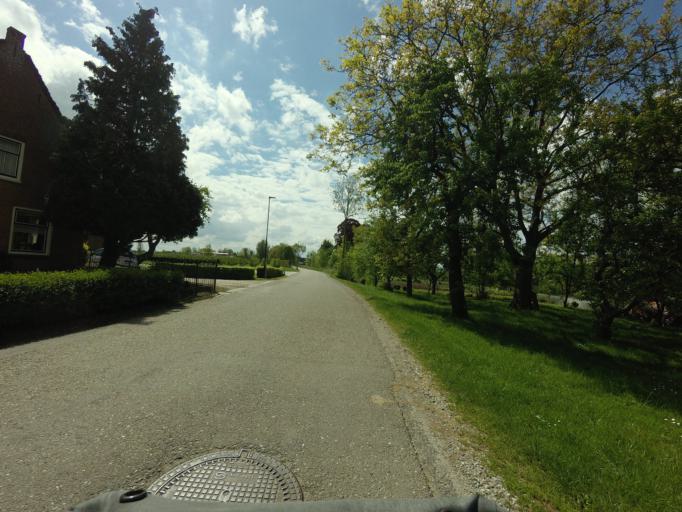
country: NL
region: South Holland
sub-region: Gemeente Giessenlanden
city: Giessenburg
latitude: 51.8968
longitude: 4.9315
